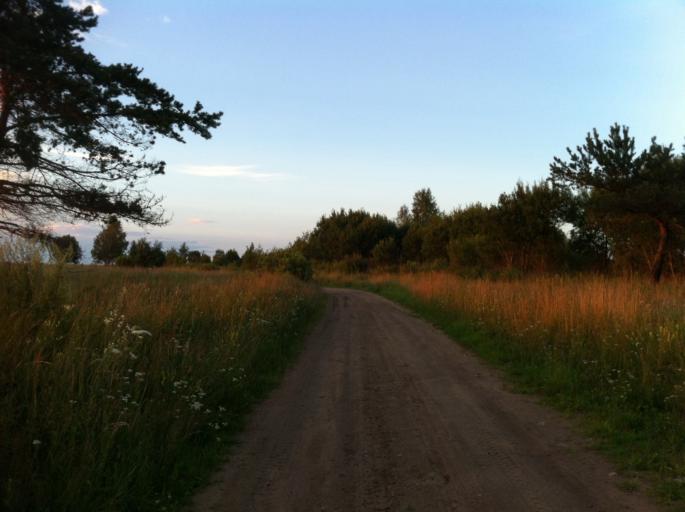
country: RU
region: Pskov
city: Izborsk
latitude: 57.8232
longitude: 27.9675
